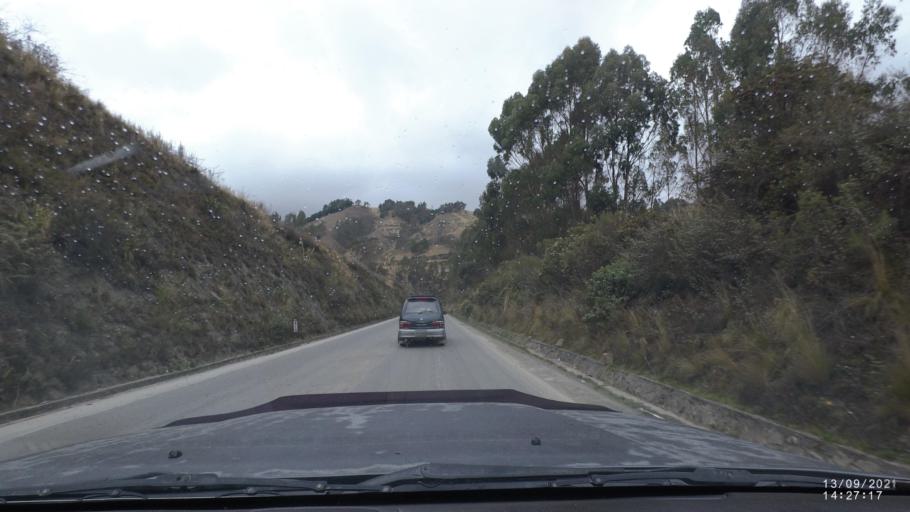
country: BO
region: Cochabamba
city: Colomi
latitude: -17.3130
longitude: -65.8633
